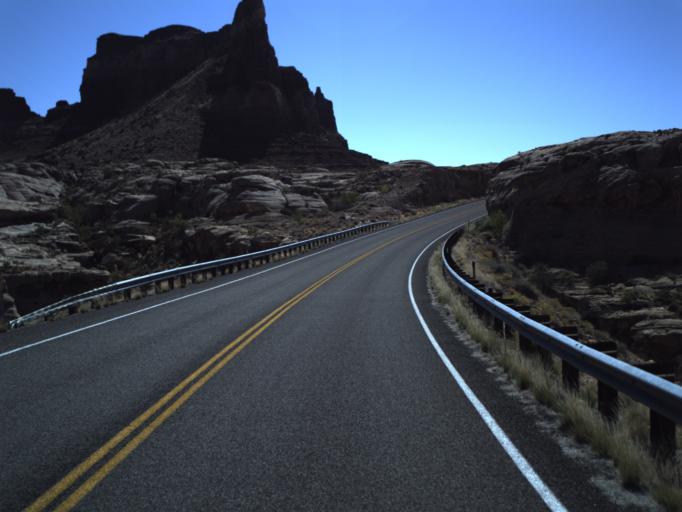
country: US
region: Utah
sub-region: San Juan County
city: Blanding
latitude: 37.9043
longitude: -110.3797
